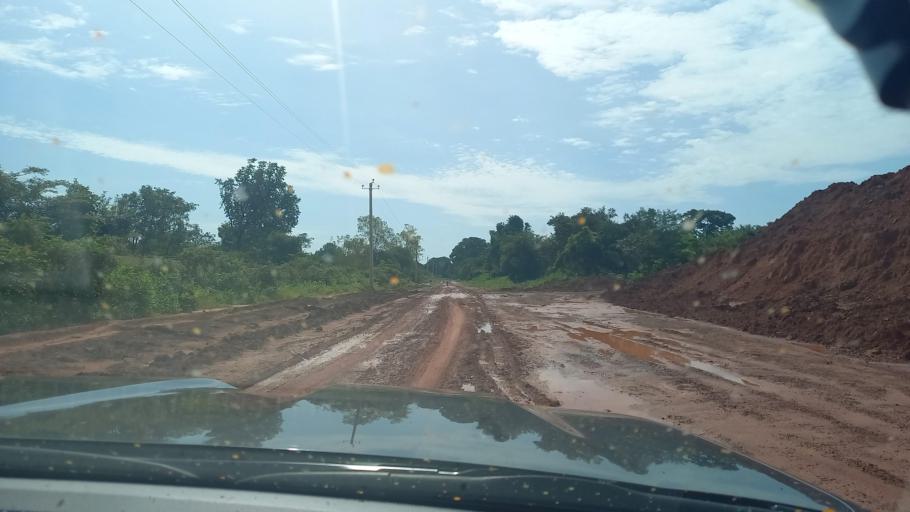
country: SN
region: Ziguinchor
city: Ziguinchor
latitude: 12.6704
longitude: -16.1887
